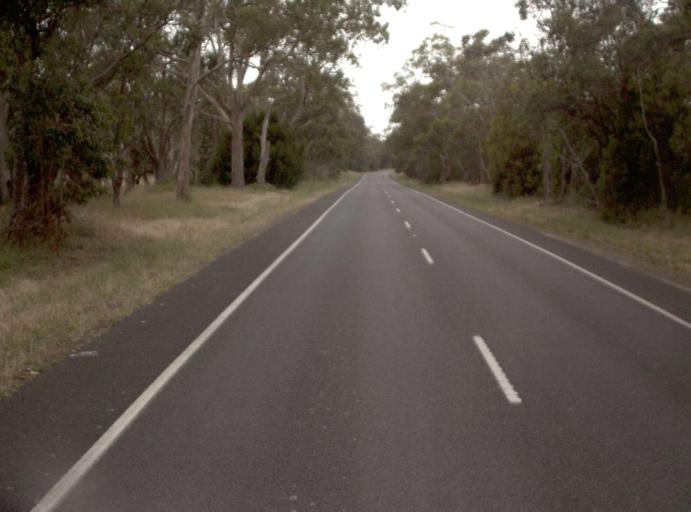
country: AU
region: Victoria
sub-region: Latrobe
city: Traralgon
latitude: -38.5452
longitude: 146.8320
